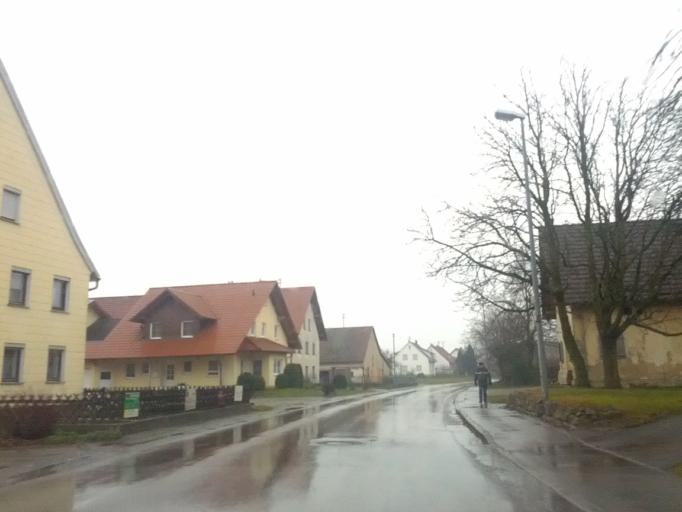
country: DE
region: Baden-Wuerttemberg
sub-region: Tuebingen Region
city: Erlenmoos
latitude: 48.0539
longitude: 9.9775
